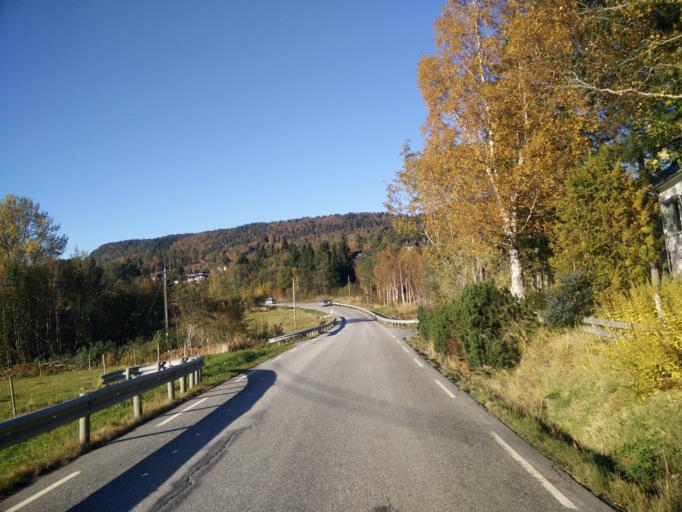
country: NO
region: More og Romsdal
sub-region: Halsa
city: Liaboen
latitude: 63.1148
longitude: 8.3211
